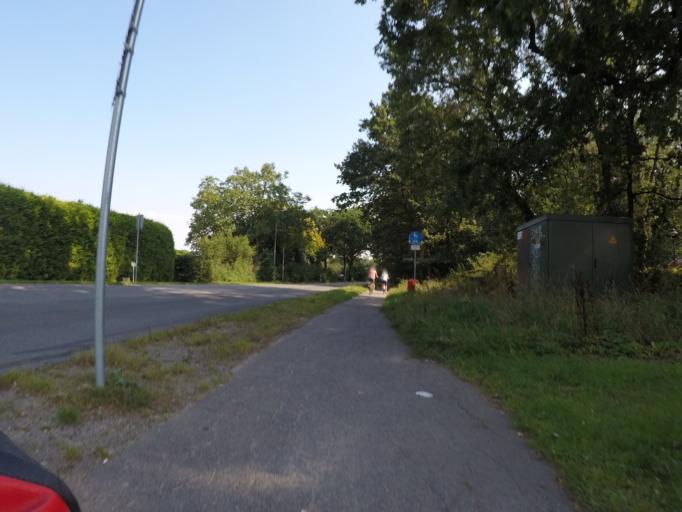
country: DE
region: Schleswig-Holstein
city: Wahlstedt
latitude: 53.9507
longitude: 10.2203
